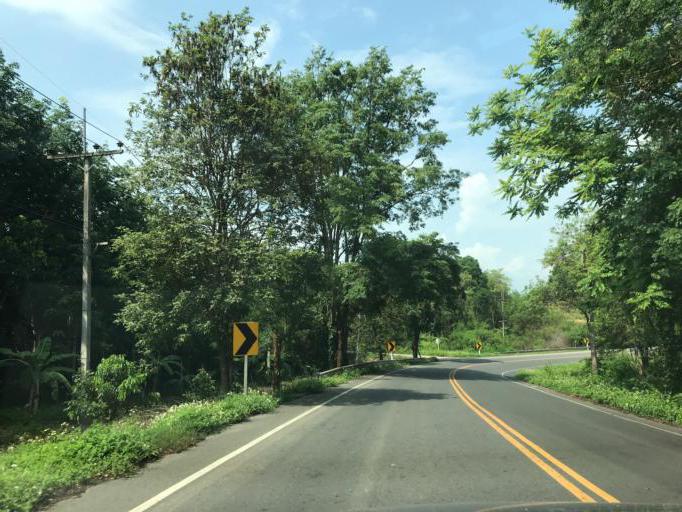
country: TH
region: Phayao
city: Pong
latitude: 19.1849
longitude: 100.2819
